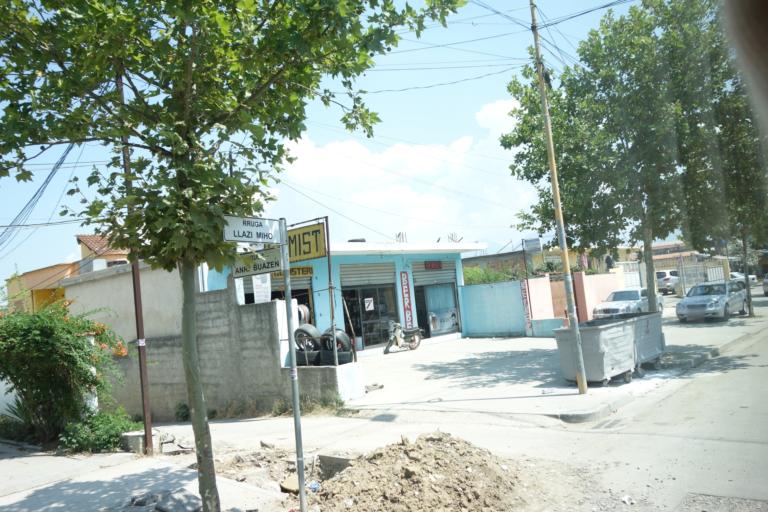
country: AL
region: Tirane
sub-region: Rrethi i Tiranes
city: Vaqarr
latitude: 41.3179
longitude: 19.7776
